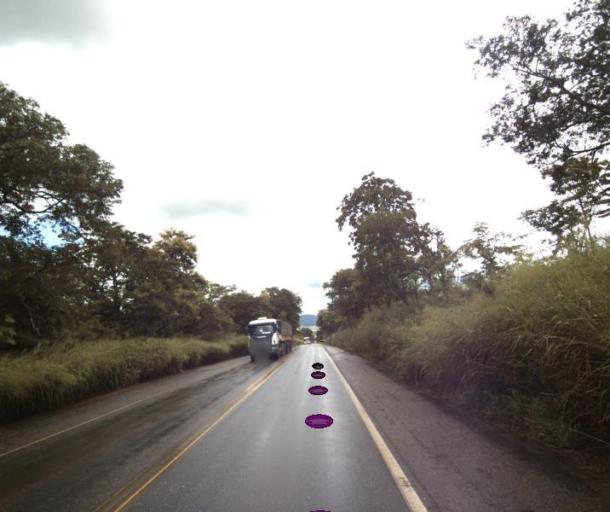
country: BR
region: Goias
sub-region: Pirenopolis
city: Pirenopolis
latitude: -16.0521
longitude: -49.0714
